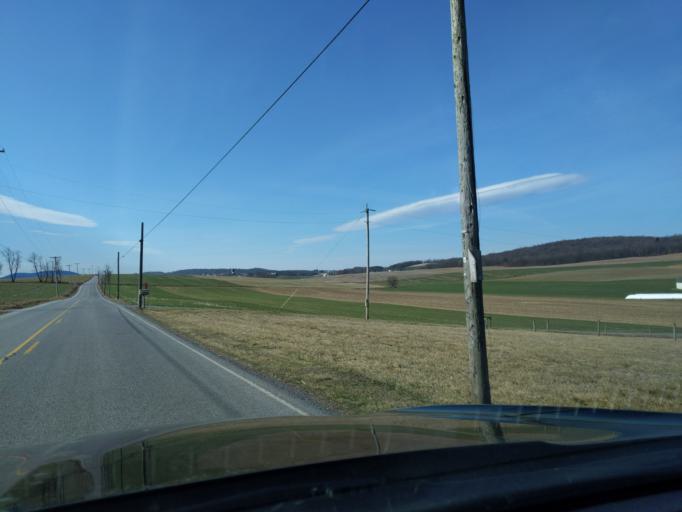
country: US
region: Pennsylvania
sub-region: Blair County
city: Martinsburg
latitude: 40.3331
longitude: -78.2648
